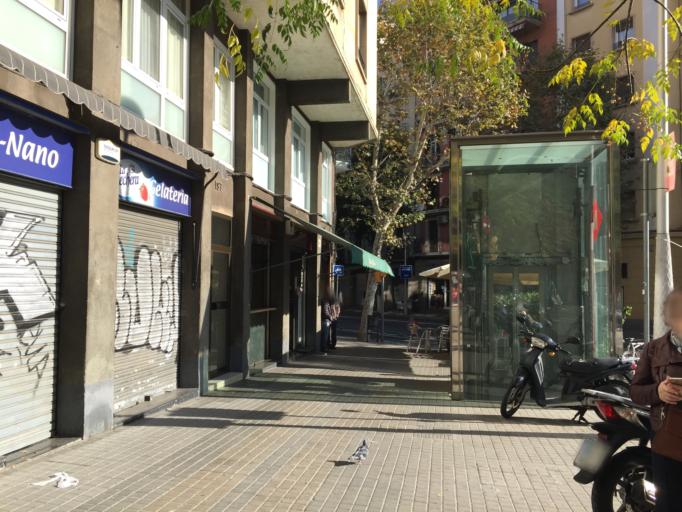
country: ES
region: Catalonia
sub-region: Provincia de Barcelona
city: Horta-Guinardo
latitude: 41.4112
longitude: 2.1766
